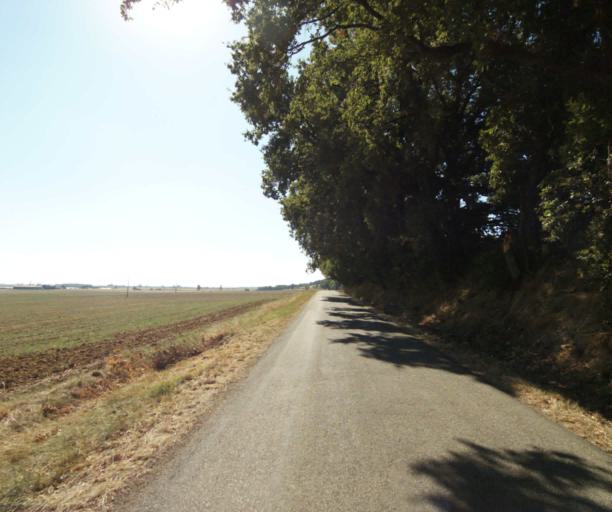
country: FR
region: Midi-Pyrenees
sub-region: Departement du Tarn-et-Garonne
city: Verdun-sur-Garonne
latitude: 43.8348
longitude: 1.2039
